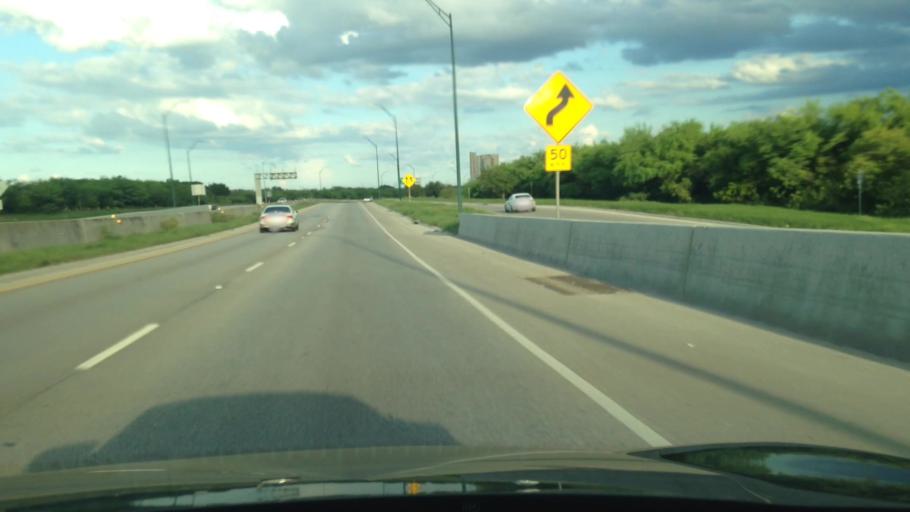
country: US
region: Texas
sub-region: Bexar County
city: Windcrest
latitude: 29.5365
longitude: -98.4098
